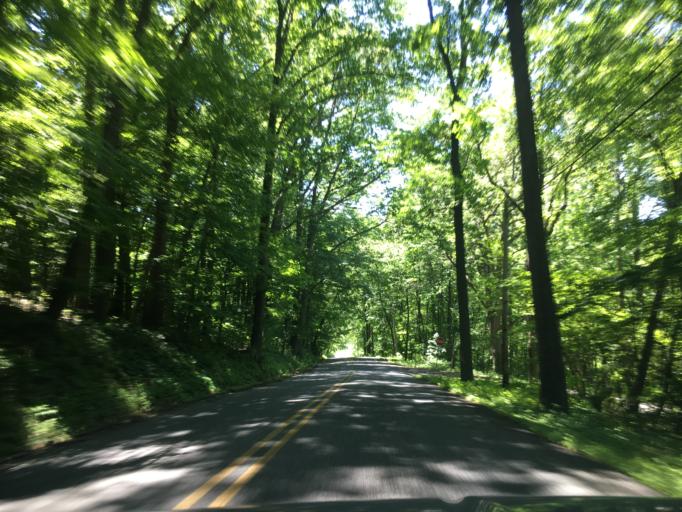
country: US
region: Pennsylvania
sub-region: Berks County
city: New Berlinville
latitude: 40.3680
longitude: -75.6595
